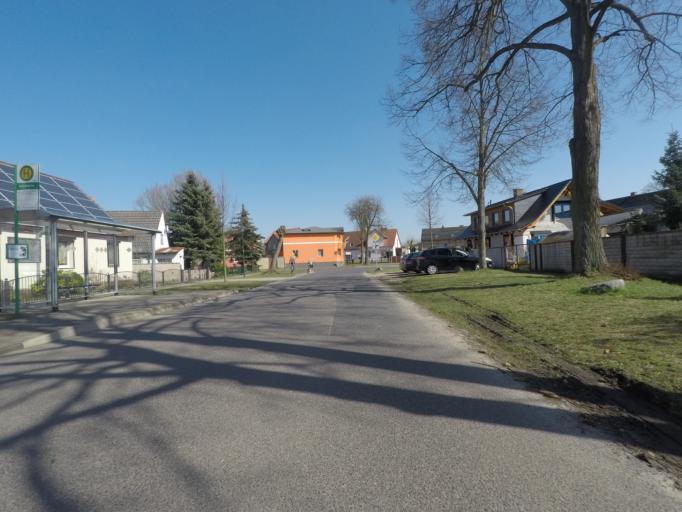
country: DE
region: Brandenburg
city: Melchow
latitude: 52.8532
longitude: 13.6810
